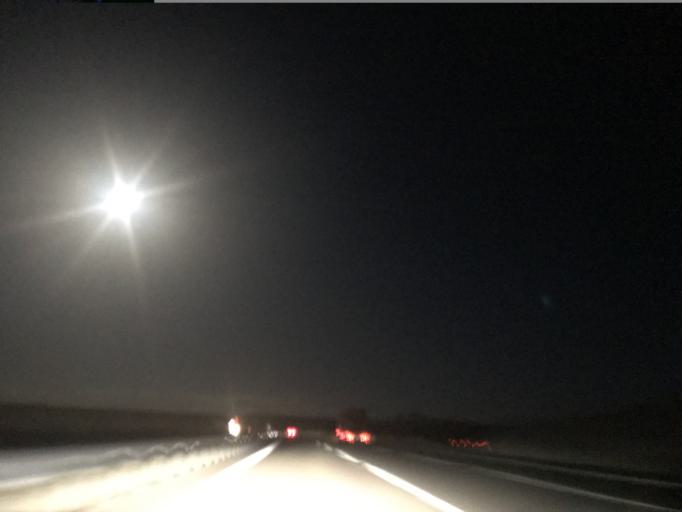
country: TR
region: Nigde
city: Ulukisla
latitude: 37.6408
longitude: 34.3824
